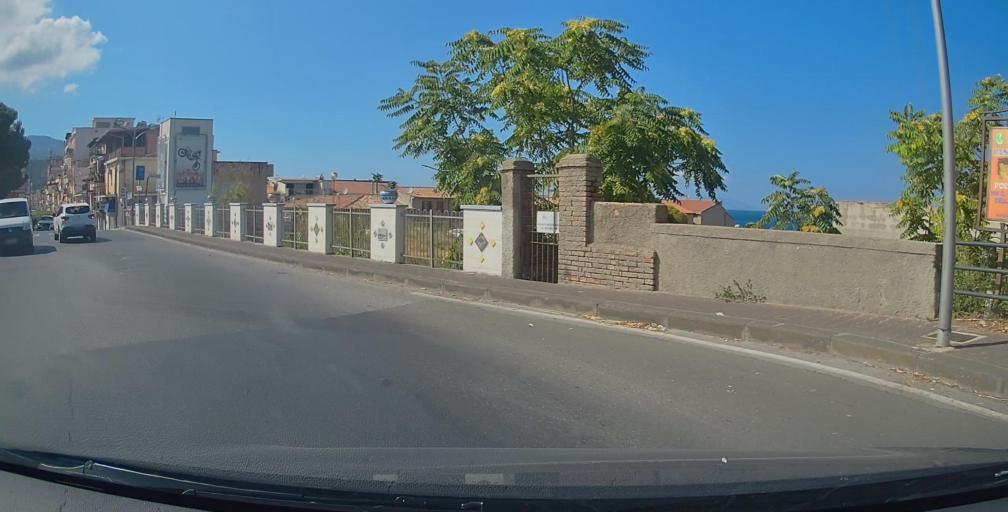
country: IT
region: Sicily
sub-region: Messina
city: Patti
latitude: 38.1506
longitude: 14.9722
